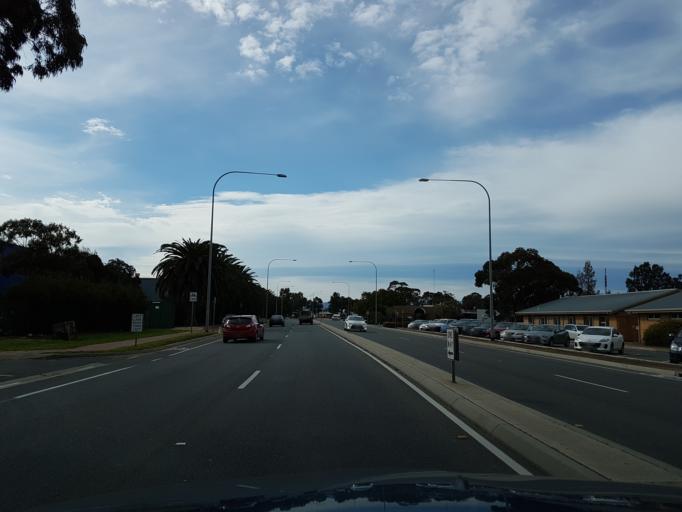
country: AU
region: South Australia
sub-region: City of West Torrens
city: Plympton
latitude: -34.9352
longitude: 138.5368
